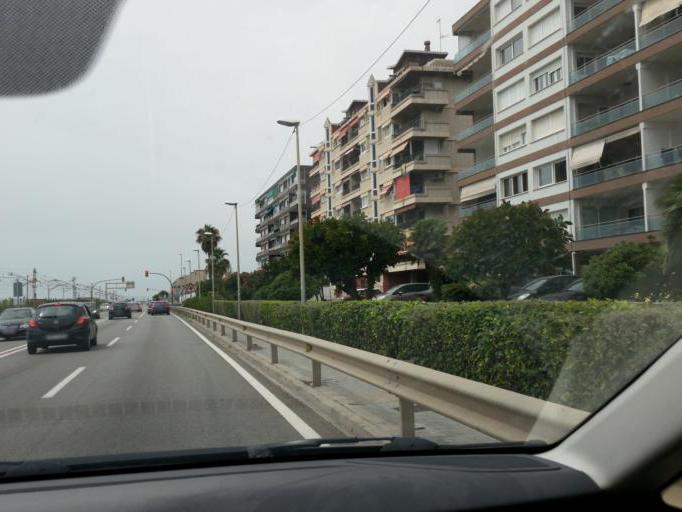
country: ES
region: Catalonia
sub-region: Provincia de Barcelona
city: Vilassar de Mar
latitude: 41.4993
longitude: 2.3864
